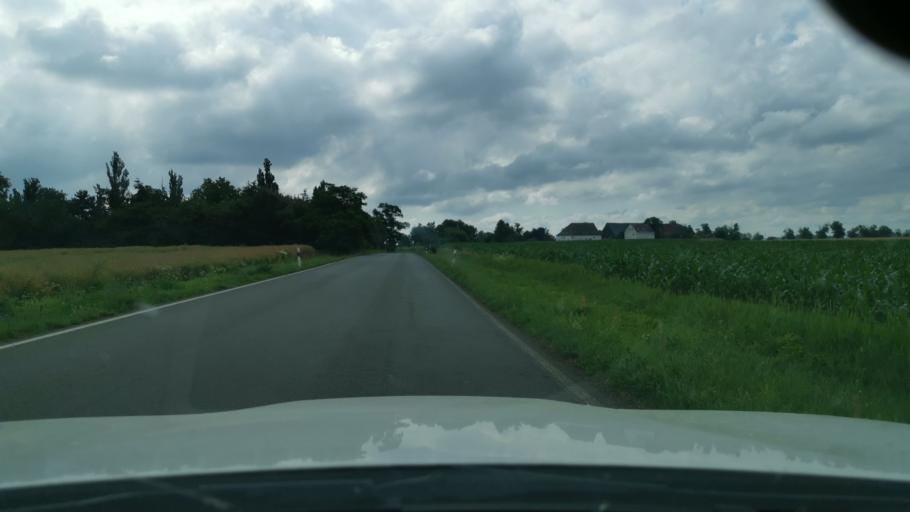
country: DE
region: Saxony
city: Torgau
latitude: 51.6176
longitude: 13.0107
